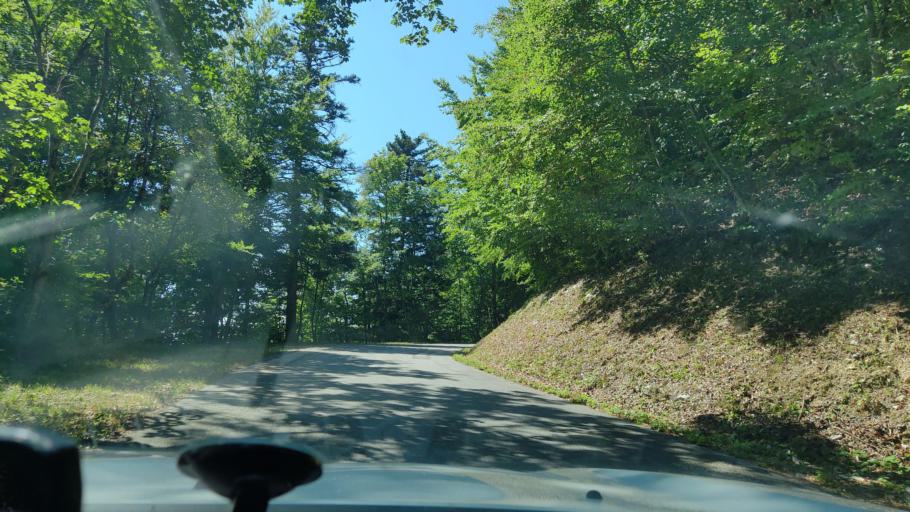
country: FR
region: Rhone-Alpes
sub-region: Departement de la Savoie
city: Le Bourget-du-Lac
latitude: 45.6563
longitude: 5.8313
